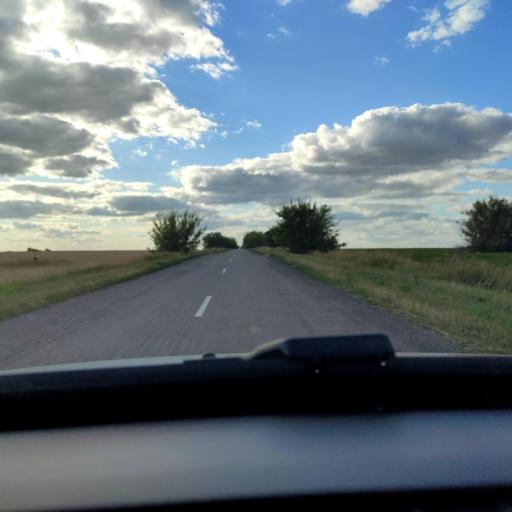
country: RU
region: Voronezj
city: Orlovo
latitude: 51.6260
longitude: 39.7791
